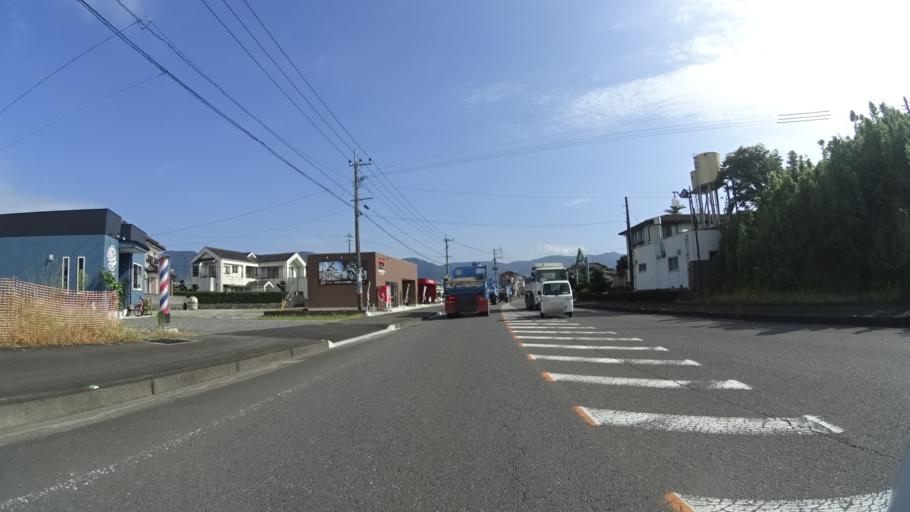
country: JP
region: Kagoshima
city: Okuchi-shinohara
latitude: 32.0445
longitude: 130.7630
